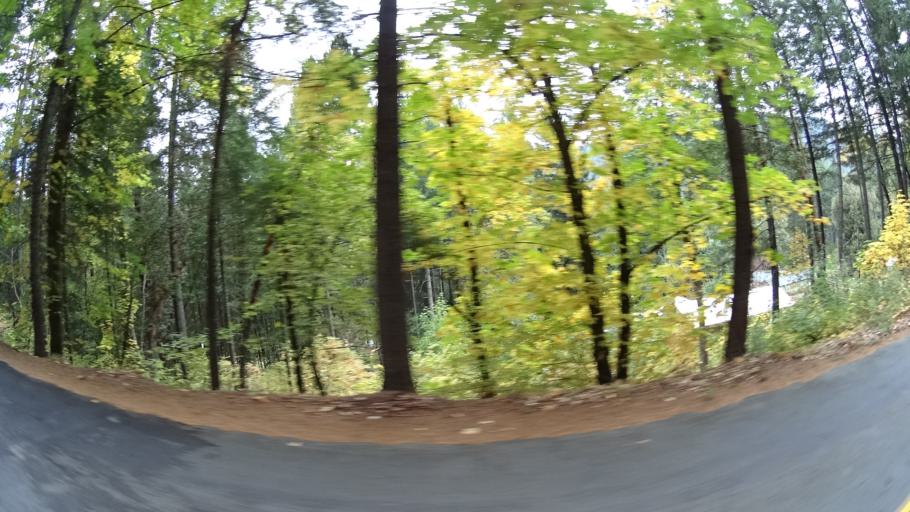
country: US
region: California
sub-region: Siskiyou County
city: Happy Camp
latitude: 41.7834
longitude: -123.3884
